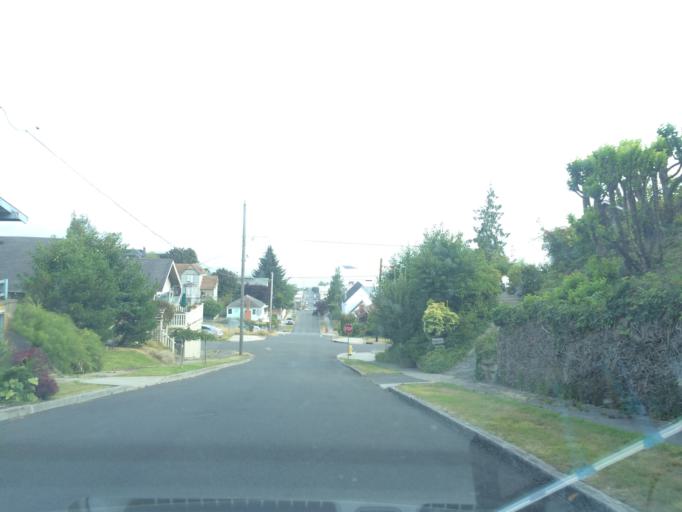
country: US
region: Oregon
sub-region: Clatsop County
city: Astoria
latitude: 46.1836
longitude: -123.8329
